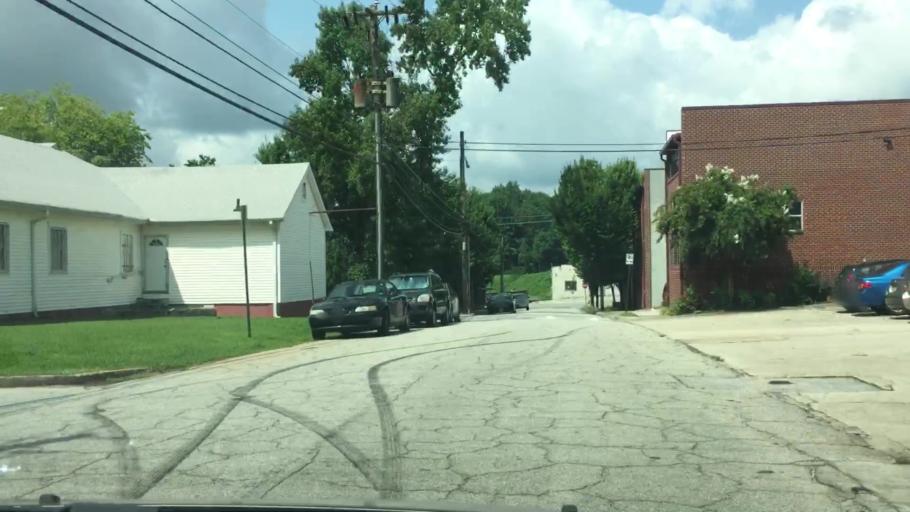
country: US
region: Georgia
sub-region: Fulton County
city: Atlanta
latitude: 33.7258
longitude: -84.3672
